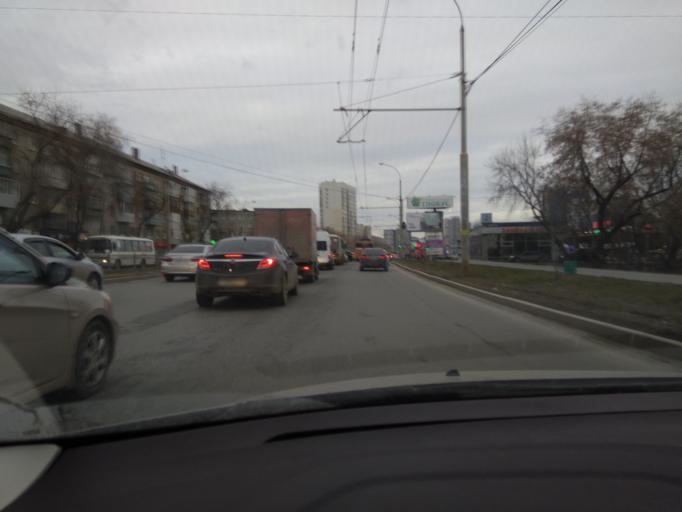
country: RU
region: Sverdlovsk
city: Yekaterinburg
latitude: 56.7863
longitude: 60.6493
